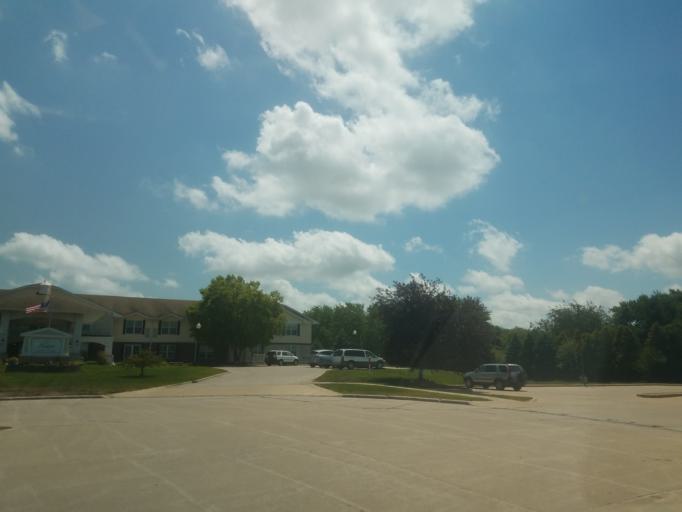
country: US
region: Illinois
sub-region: McLean County
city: Bloomington
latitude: 40.4814
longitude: -88.9396
